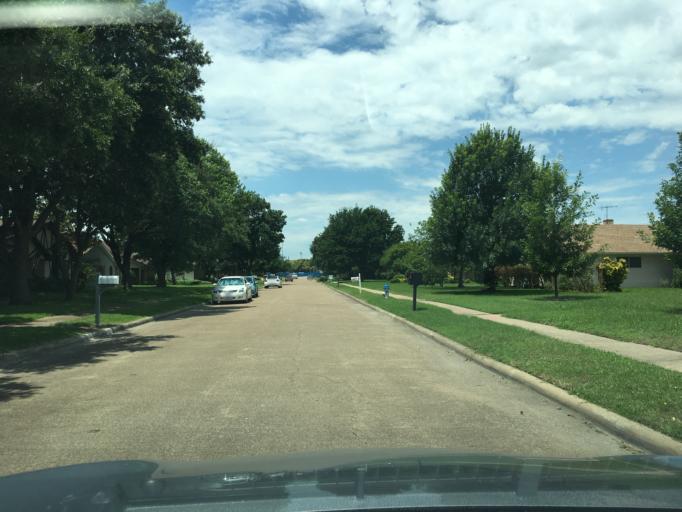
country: US
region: Texas
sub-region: Dallas County
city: Richardson
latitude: 32.9353
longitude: -96.6879
